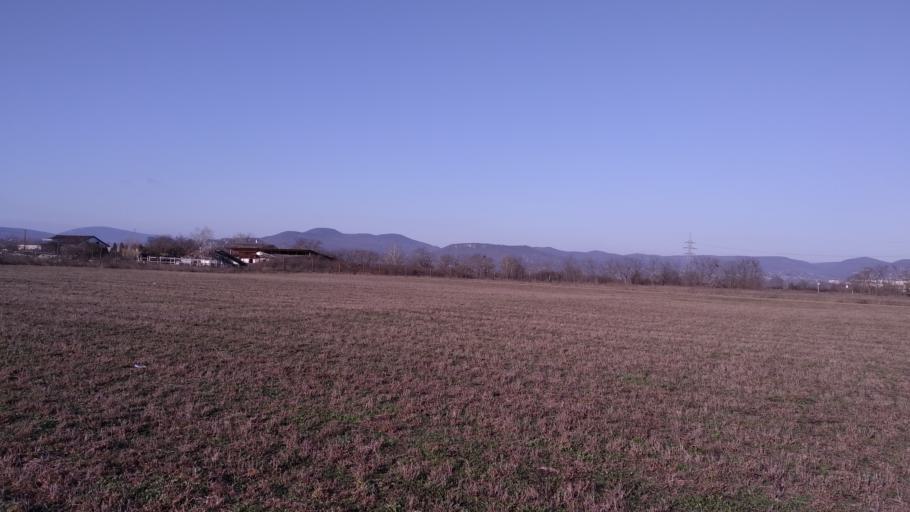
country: HU
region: Pest
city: Budakalasz
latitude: 47.6330
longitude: 19.0659
